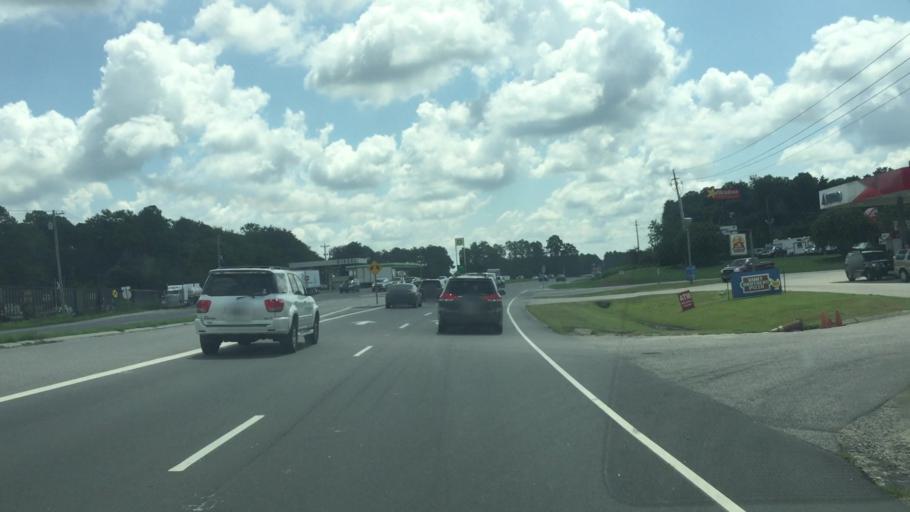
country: US
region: North Carolina
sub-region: Scotland County
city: Laurel Hill
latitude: 34.8075
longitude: -79.5454
